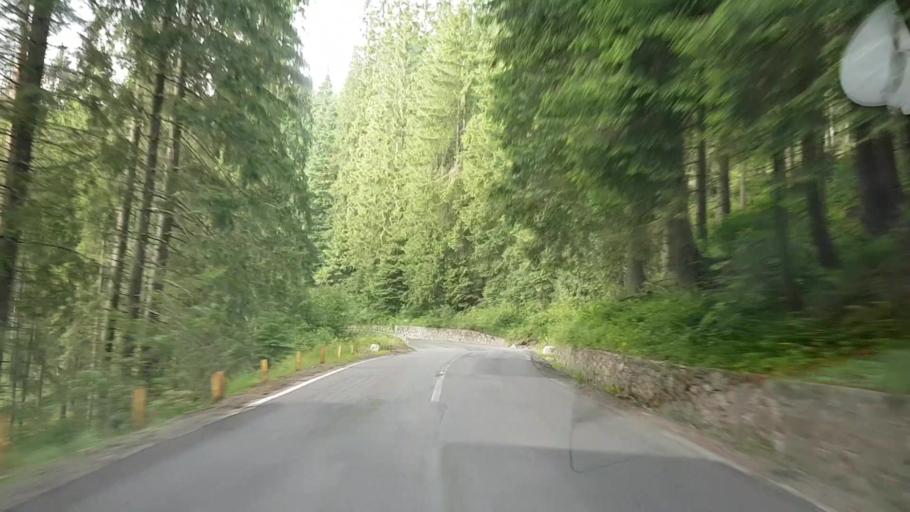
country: RO
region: Harghita
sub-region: Municipiul Gheorgheni
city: Gheorgheni
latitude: 46.7784
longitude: 25.7293
